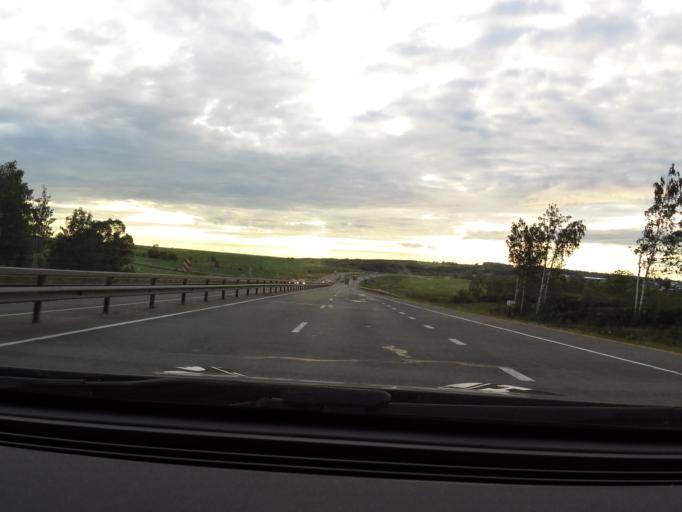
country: RU
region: Chuvashia
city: Kugesi
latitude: 55.9762
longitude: 47.3616
